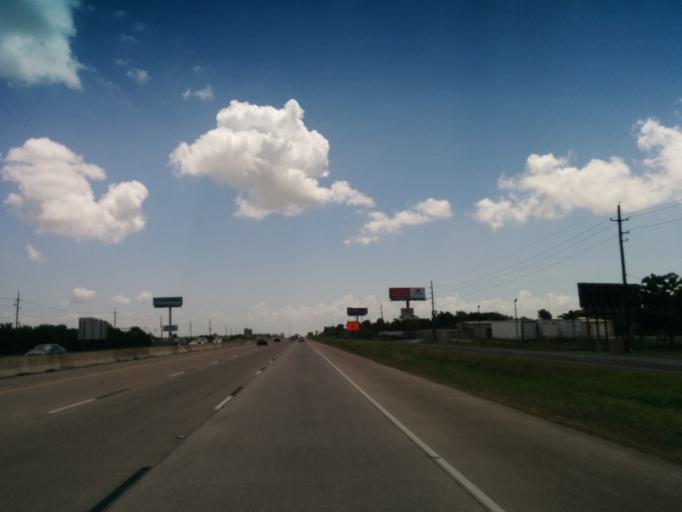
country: US
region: Texas
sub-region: Chambers County
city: Mont Belvieu
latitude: 29.8231
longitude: -94.8801
